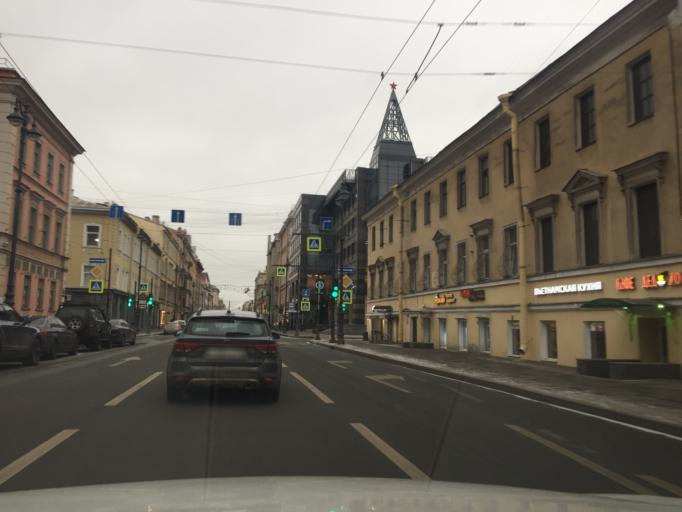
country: RU
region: St.-Petersburg
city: Petrogradka
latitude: 59.9603
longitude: 30.3030
